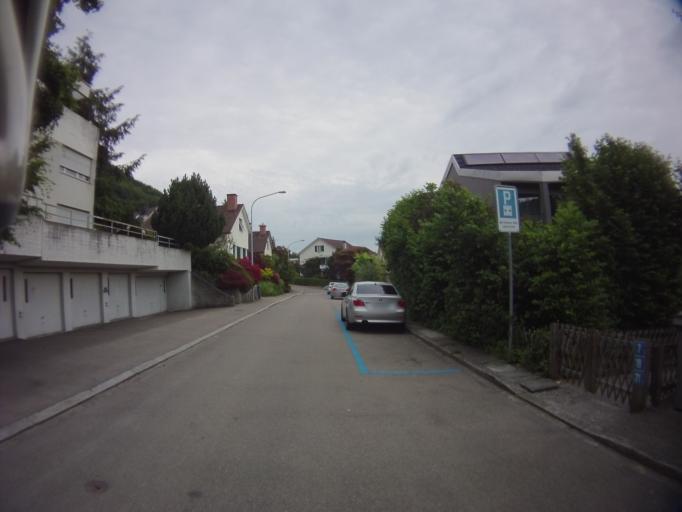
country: CH
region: Zurich
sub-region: Bezirk Zuerich
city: Zuerich (Kreis 2) / Unter-Leimbach
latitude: 47.3349
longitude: 8.5162
